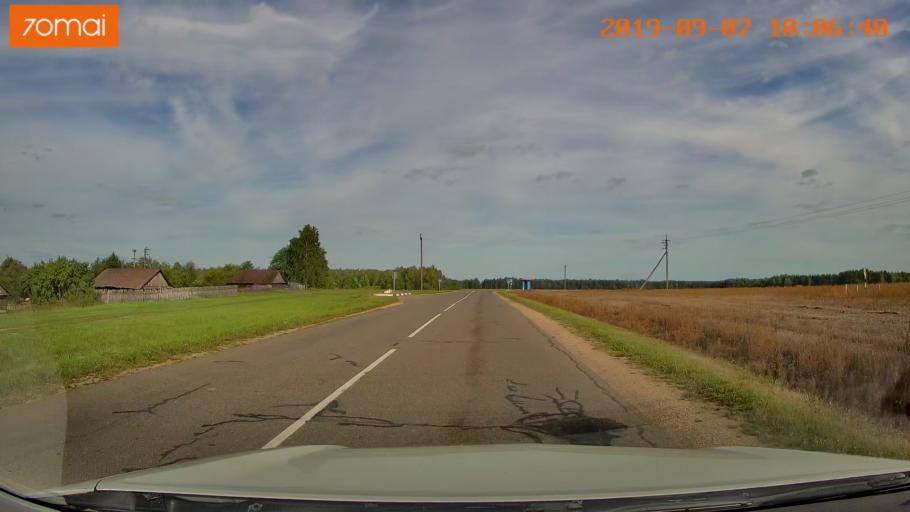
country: BY
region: Grodnenskaya
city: Voranava
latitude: 54.0651
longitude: 25.4024
